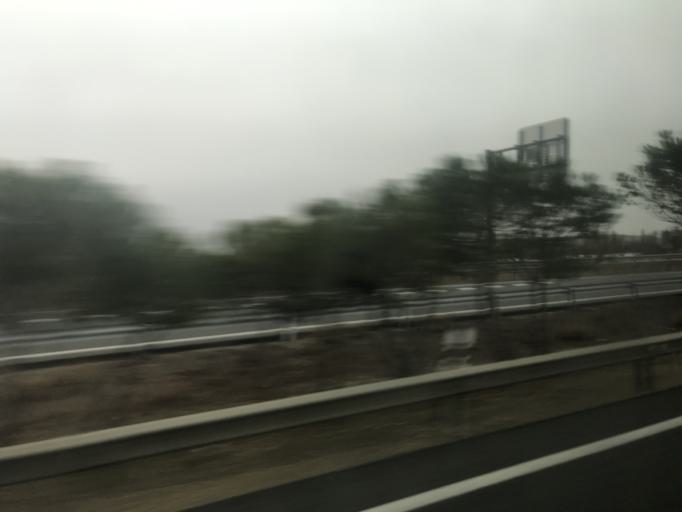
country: ES
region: Castille and Leon
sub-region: Provincia de Burgos
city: Villaquiran de los Infantes
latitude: 42.2128
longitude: -4.0073
